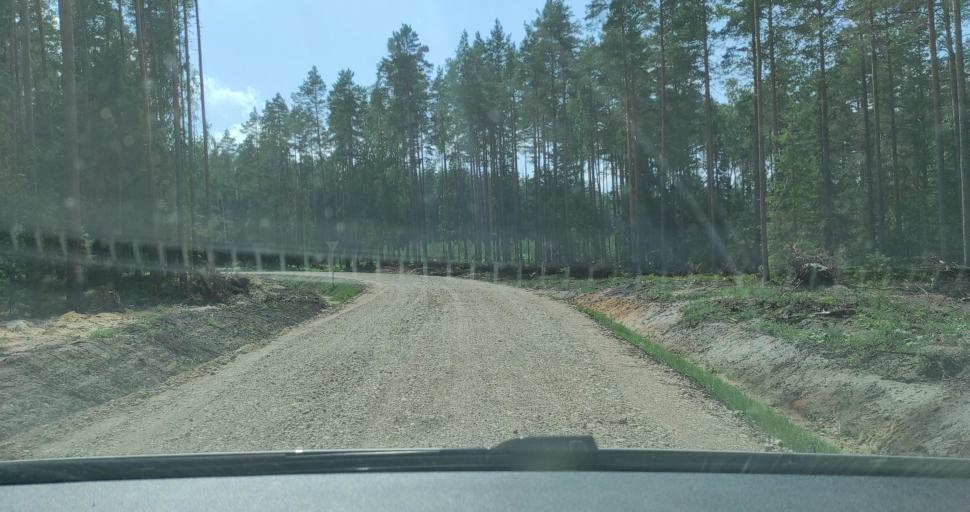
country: LV
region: Kuldigas Rajons
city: Kuldiga
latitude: 57.0666
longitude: 22.1930
